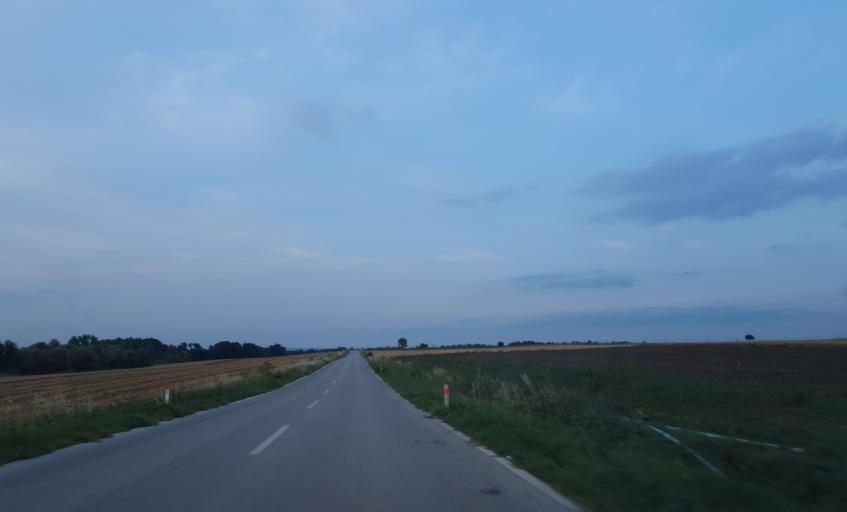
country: TR
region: Tekirdag
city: Beyazkoy
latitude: 41.3986
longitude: 27.6363
